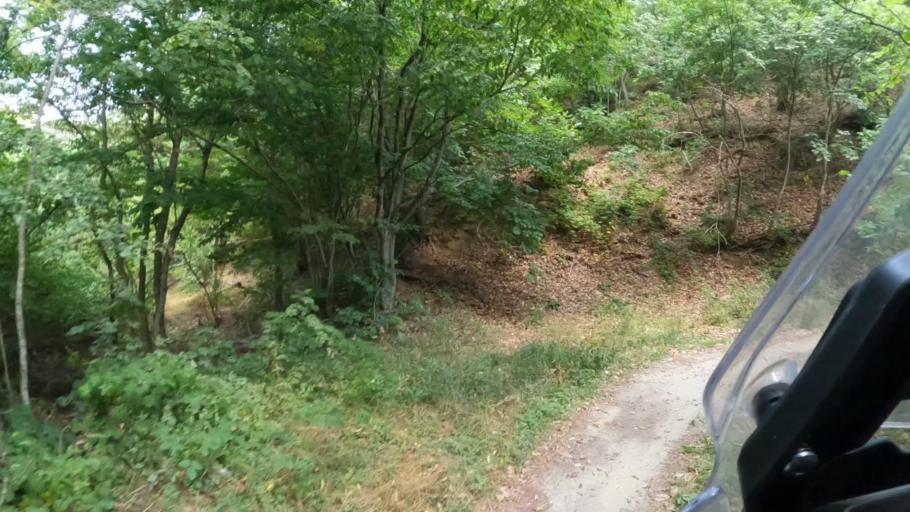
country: IT
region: Piedmont
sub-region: Provincia di Alessandria
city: Cassinelle-Concentrico
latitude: 44.5685
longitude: 8.5684
